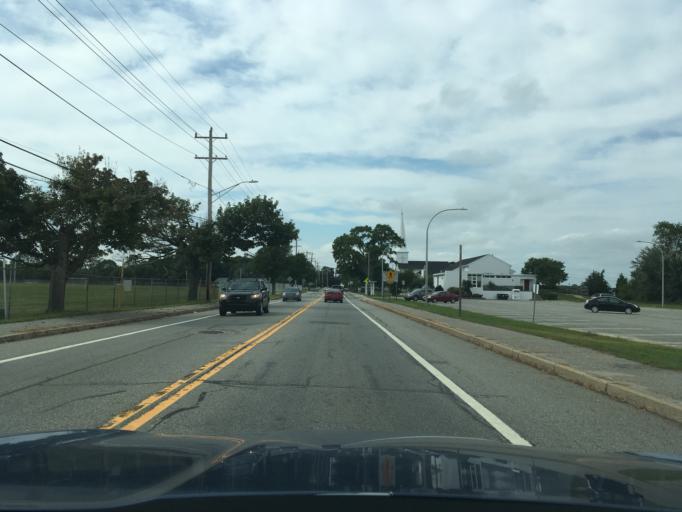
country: US
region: Rhode Island
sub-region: Bristol County
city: Barrington
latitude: 41.7472
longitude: -71.3172
